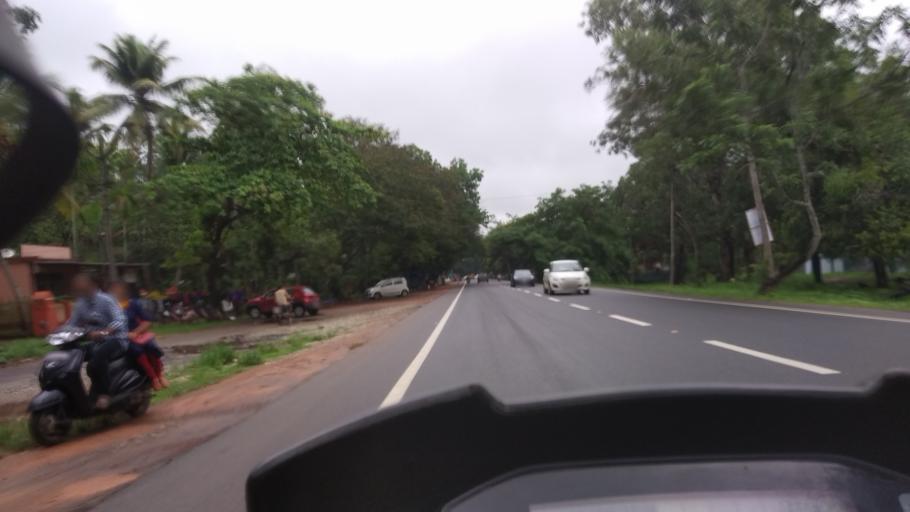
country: IN
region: Kerala
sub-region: Alappuzha
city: Mavelikara
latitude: 9.3042
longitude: 76.4325
